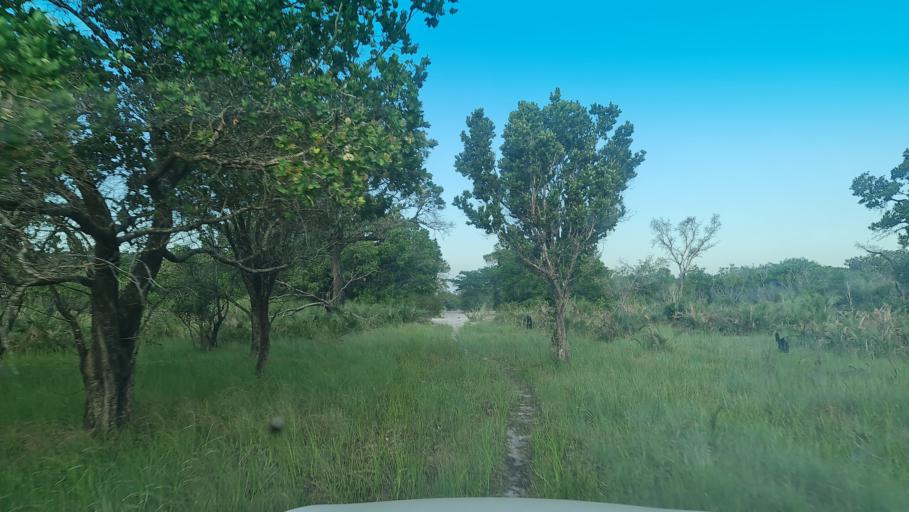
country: MZ
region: Gaza
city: Macia
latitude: -25.2168
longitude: 33.0482
